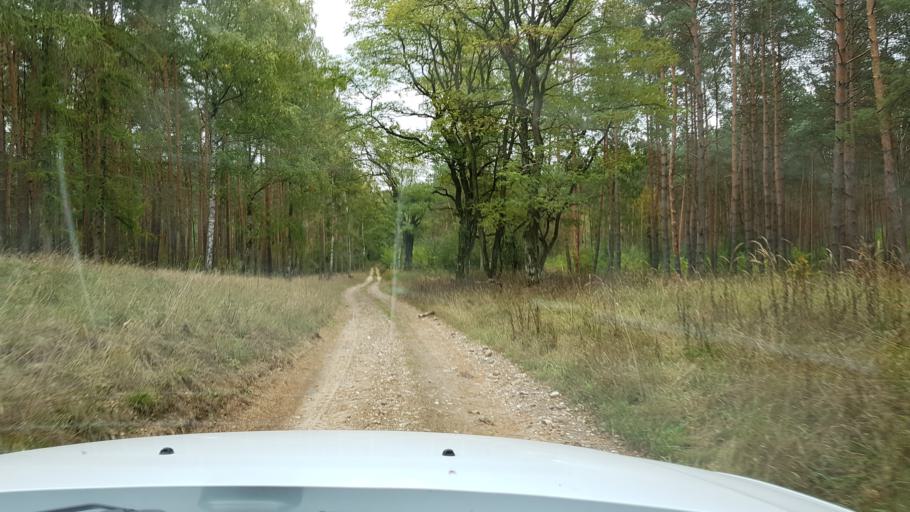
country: PL
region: West Pomeranian Voivodeship
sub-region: Powiat gryfinski
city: Cedynia
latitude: 52.8400
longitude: 14.2720
